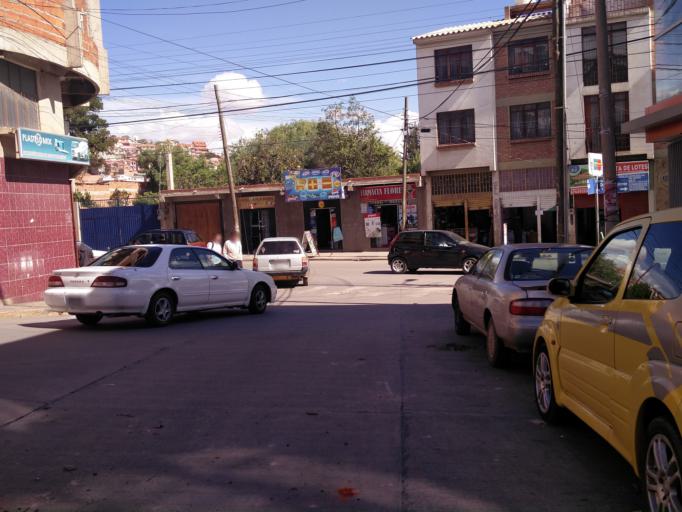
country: BO
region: Chuquisaca
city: Sucre
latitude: -19.0387
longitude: -65.2460
